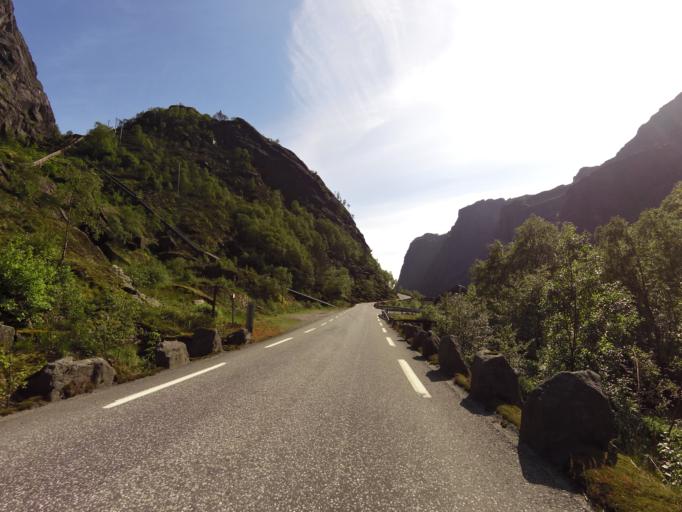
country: NO
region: Rogaland
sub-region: Sokndal
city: Hauge i Dalane
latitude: 58.3295
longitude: 6.3567
